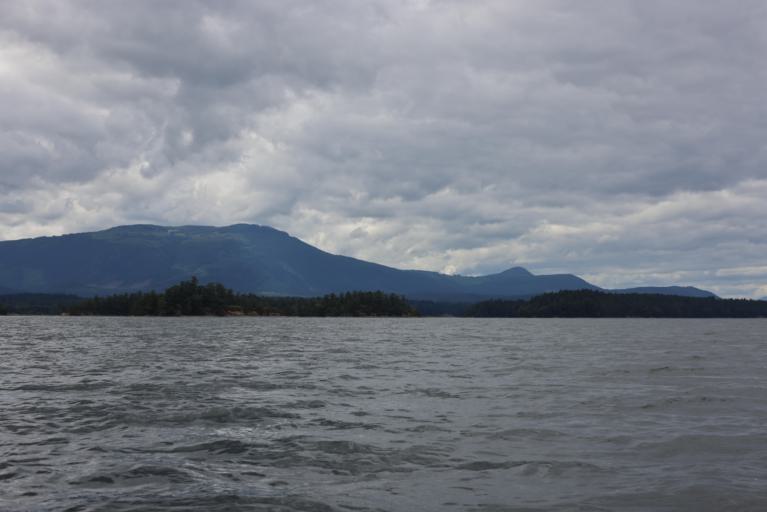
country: CA
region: British Columbia
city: North Cowichan
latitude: 48.8873
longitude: -123.6342
